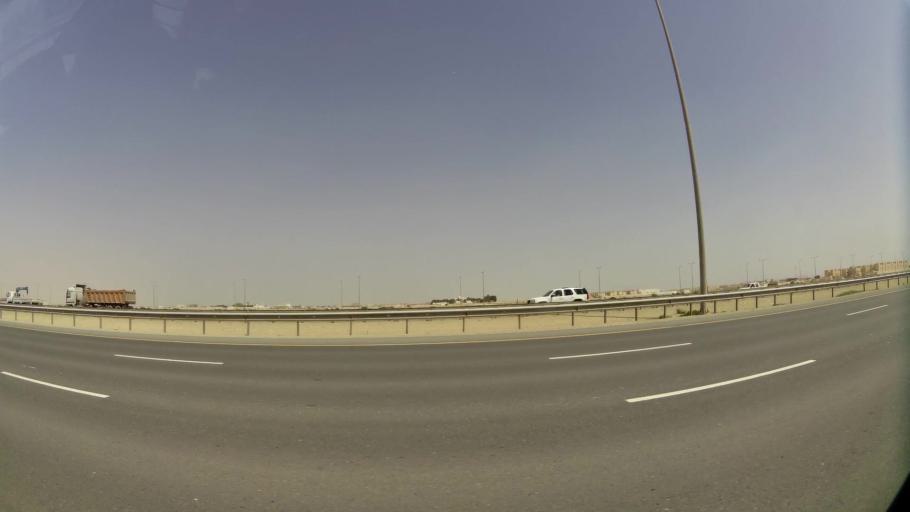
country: QA
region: Baladiyat Umm Salal
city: Umm Salal Muhammad
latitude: 25.4207
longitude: 51.4194
